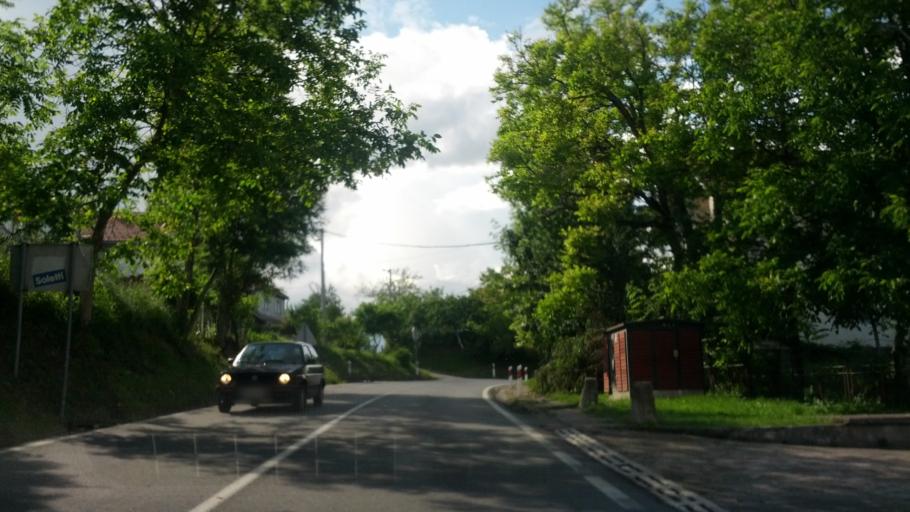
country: BA
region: Federation of Bosnia and Herzegovina
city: Izacic
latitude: 44.8731
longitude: 15.7831
